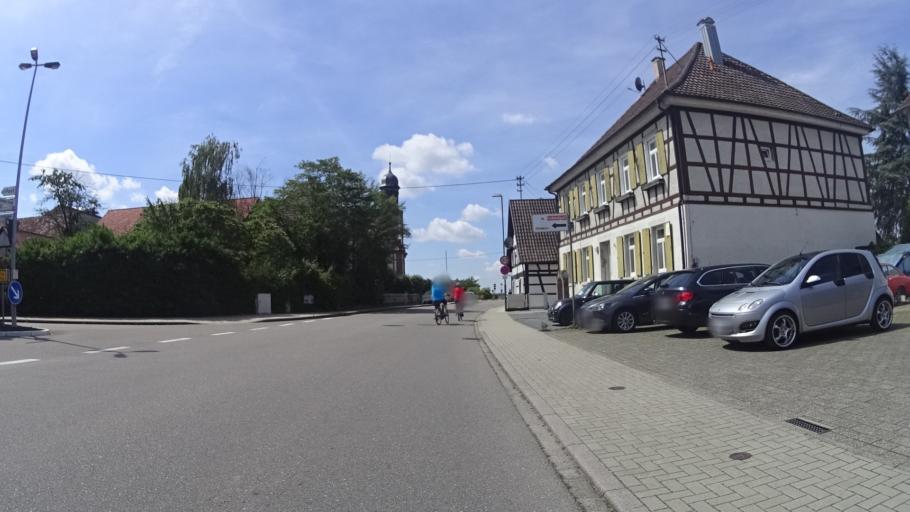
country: DE
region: Baden-Wuerttemberg
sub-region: Freiburg Region
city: Meissenheim
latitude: 48.4489
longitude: 7.8156
